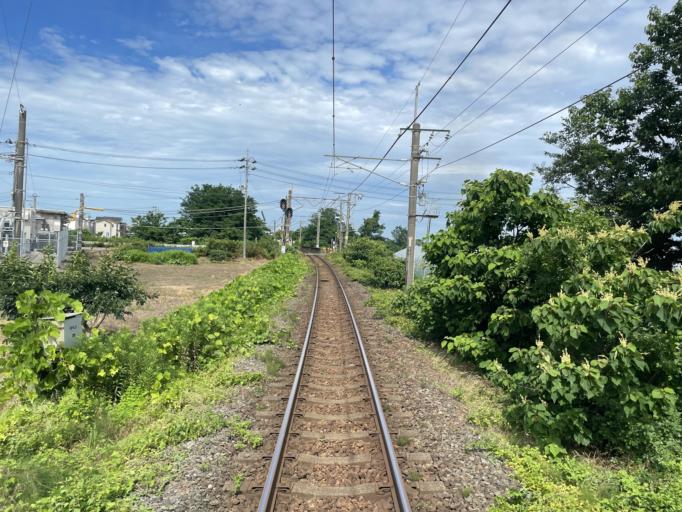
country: JP
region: Niigata
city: Kameda-honcho
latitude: 37.9236
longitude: 139.1646
